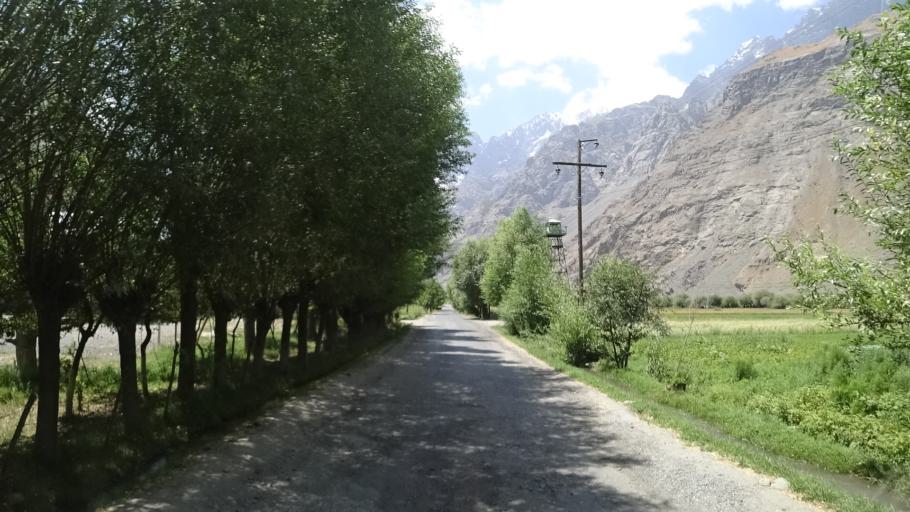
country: TJ
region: Gorno-Badakhshan
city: Rushon
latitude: 37.8682
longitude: 71.6002
